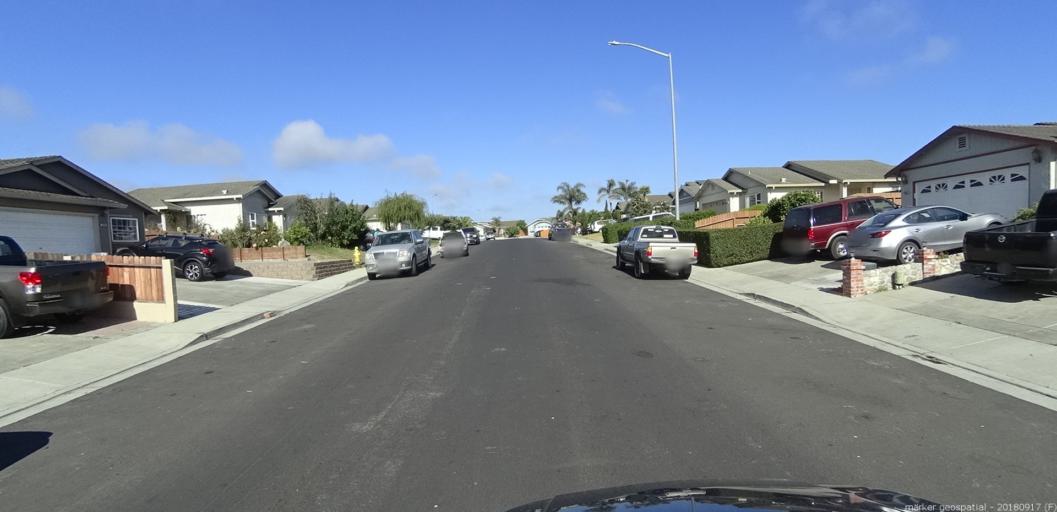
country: US
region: California
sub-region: Monterey County
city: Castroville
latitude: 36.7867
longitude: -121.7276
